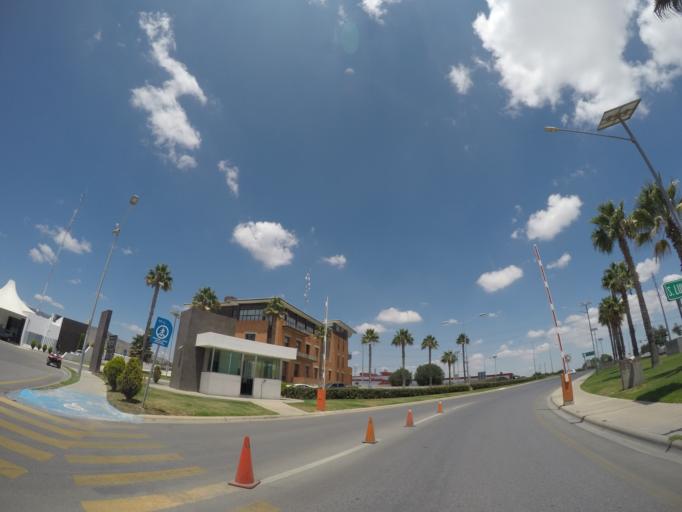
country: MX
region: San Luis Potosi
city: La Pila
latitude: 22.0410
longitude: -100.8938
